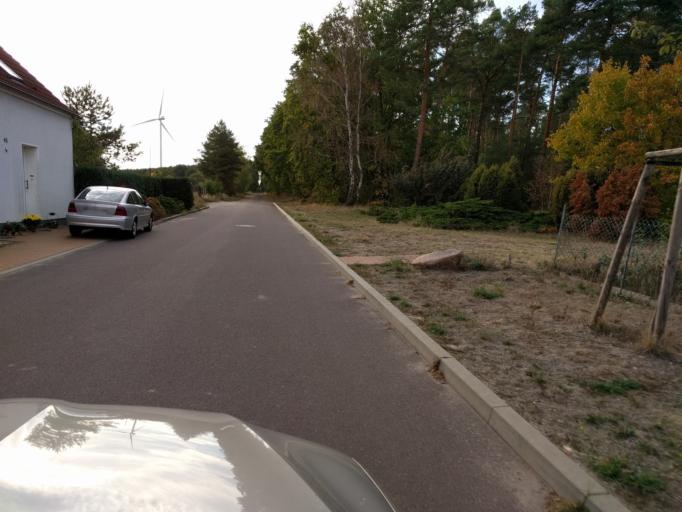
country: DE
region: Brandenburg
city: Ziesar
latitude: 52.2125
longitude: 12.2808
